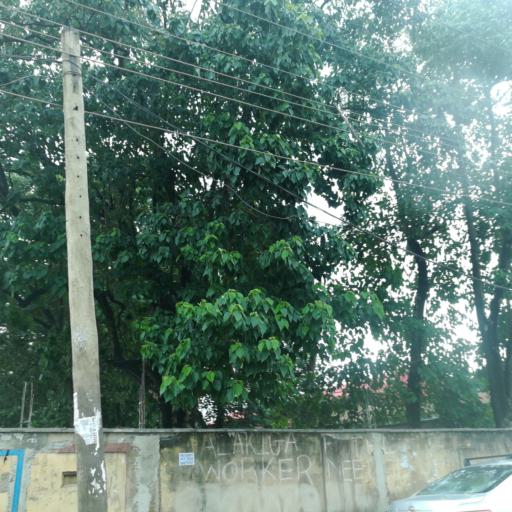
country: NG
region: Lagos
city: Oshodi
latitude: 6.5629
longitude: 3.3461
